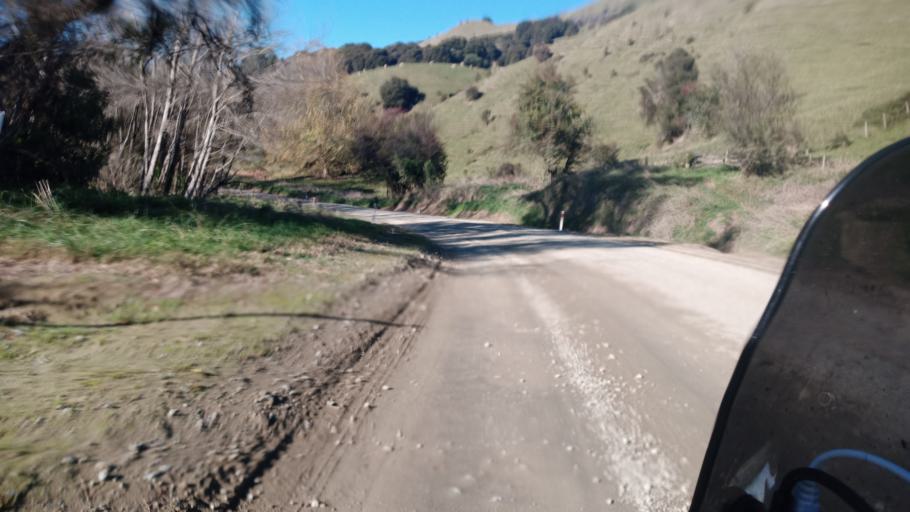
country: NZ
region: Hawke's Bay
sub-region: Wairoa District
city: Wairoa
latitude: -38.8479
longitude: 177.1660
